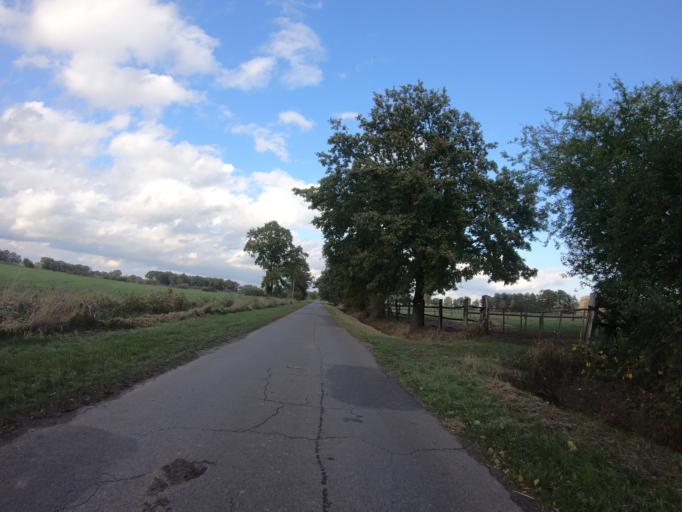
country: DE
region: Lower Saxony
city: Wagenhoff
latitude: 52.5258
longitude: 10.5409
